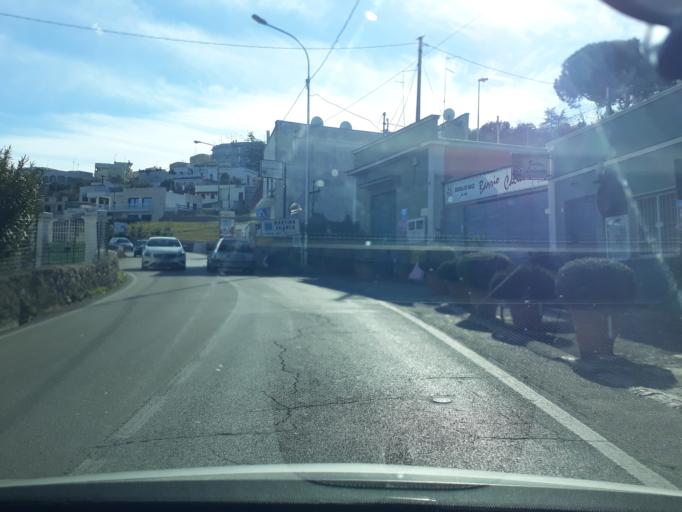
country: IT
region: Apulia
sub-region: Provincia di Taranto
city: Martina Franca
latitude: 40.7105
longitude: 17.3351
